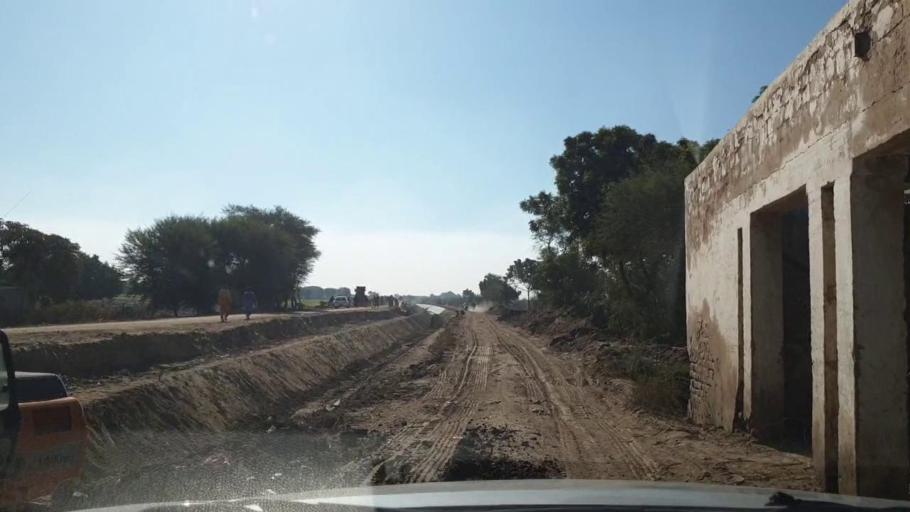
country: PK
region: Sindh
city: Jhol
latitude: 25.8201
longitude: 69.0113
